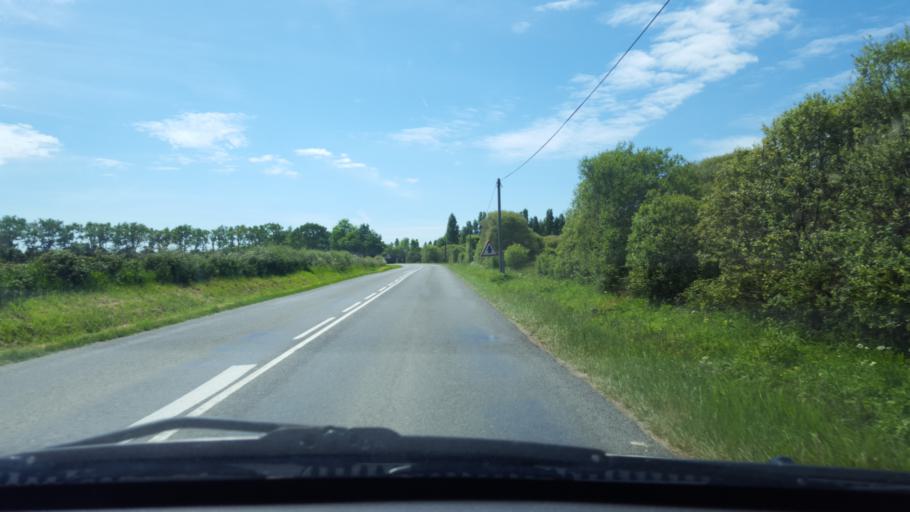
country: FR
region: Pays de la Loire
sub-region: Departement de la Loire-Atlantique
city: Saint-Philbert-de-Grand-Lieu
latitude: 47.0043
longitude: -1.6611
